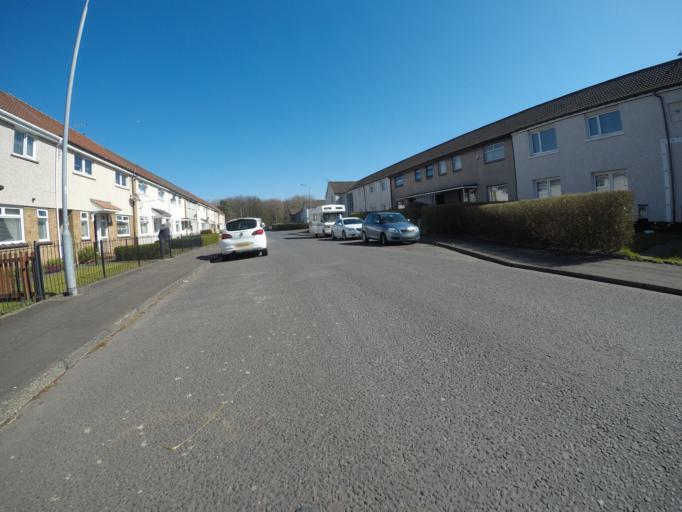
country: GB
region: Scotland
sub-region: North Ayrshire
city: Irvine
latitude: 55.6277
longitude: -4.6588
